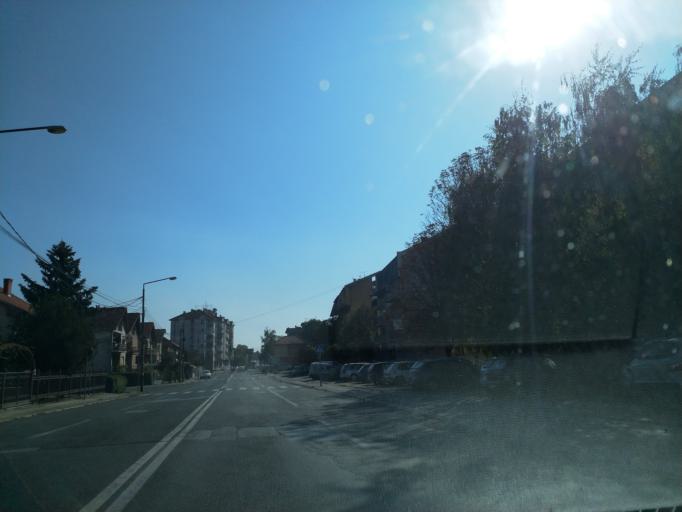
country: RS
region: Central Serbia
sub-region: Pomoravski Okrug
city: Paracin
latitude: 43.8617
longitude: 21.4214
